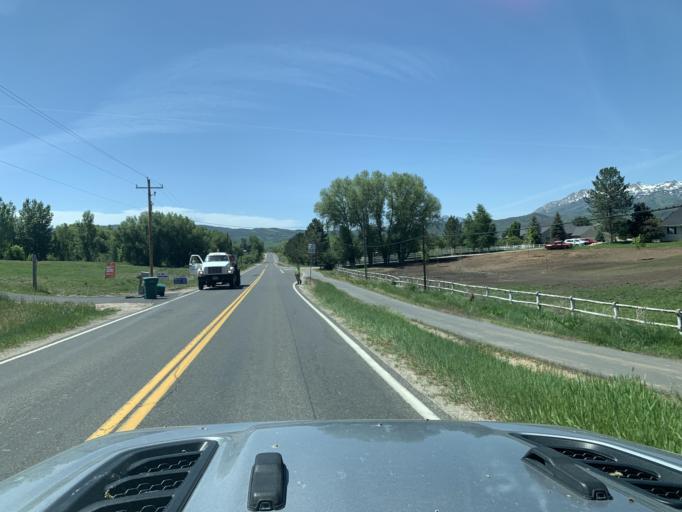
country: US
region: Utah
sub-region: Weber County
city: Wolf Creek
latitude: 41.2829
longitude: -111.7771
